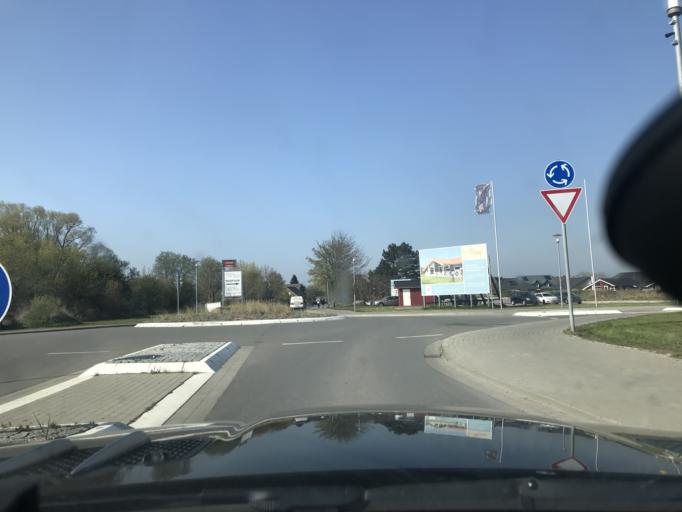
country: DE
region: Schleswig-Holstein
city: Grossenbrode
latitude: 54.3627
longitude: 11.0842
